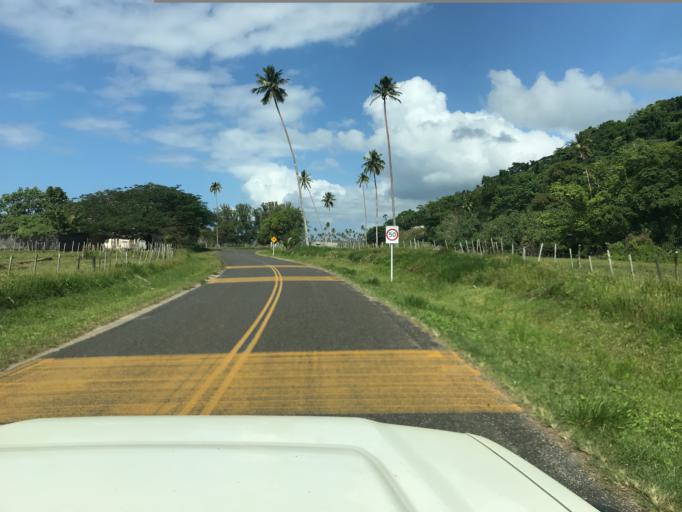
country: VU
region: Sanma
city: Luganville
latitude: -15.3369
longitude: 167.1791
